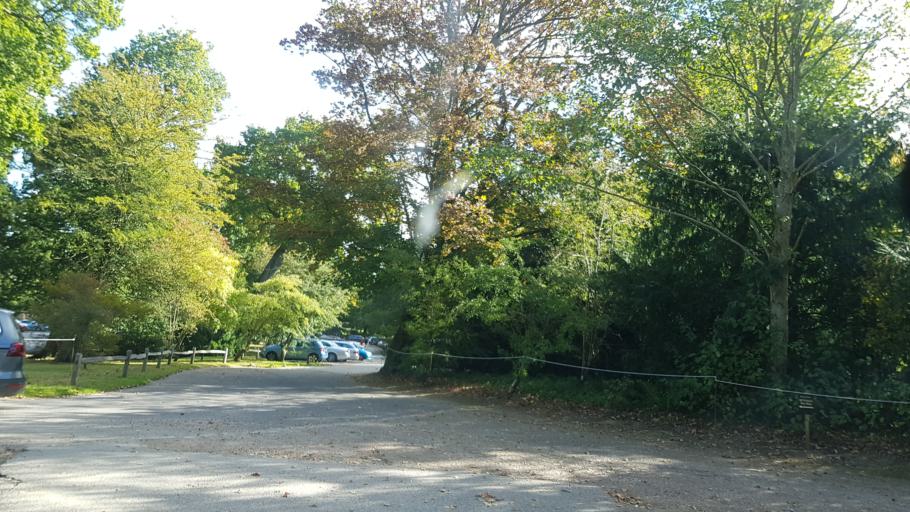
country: GB
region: England
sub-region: West Sussex
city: Petworth
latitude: 50.9944
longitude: -0.6121
